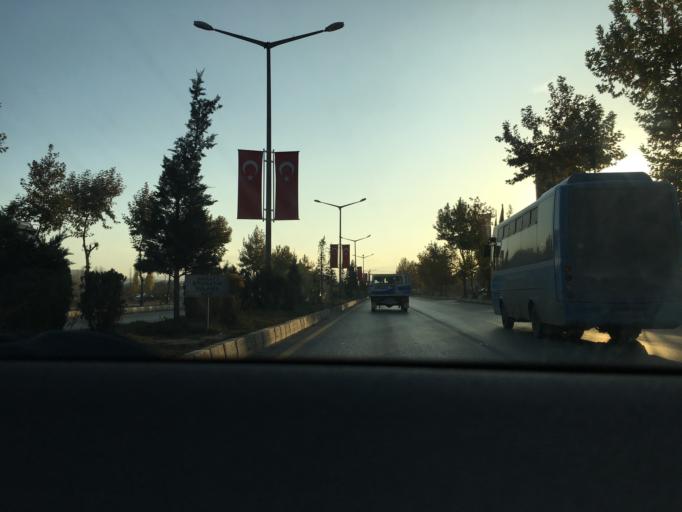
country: TR
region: Van
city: Van
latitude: 38.4808
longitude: 43.3599
